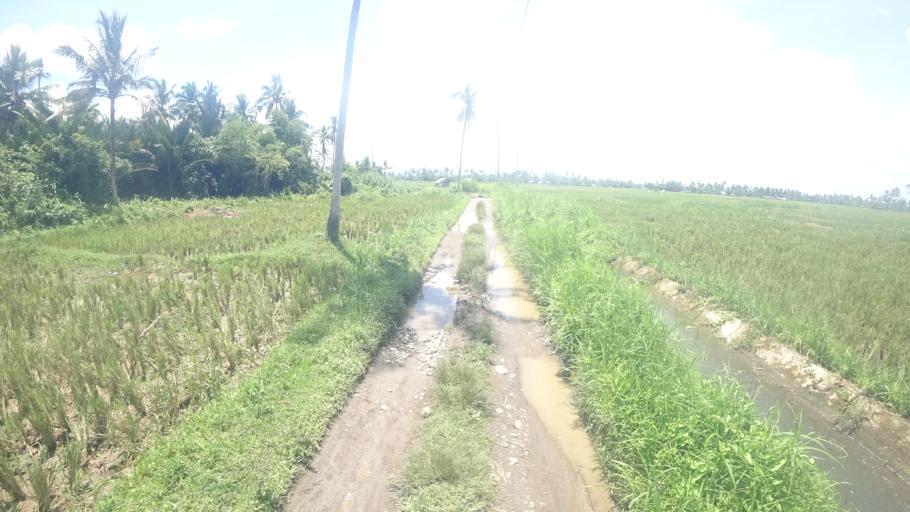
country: PH
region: Eastern Visayas
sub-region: Province of Leyte
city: Alangalang
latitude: 11.2284
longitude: 124.8410
